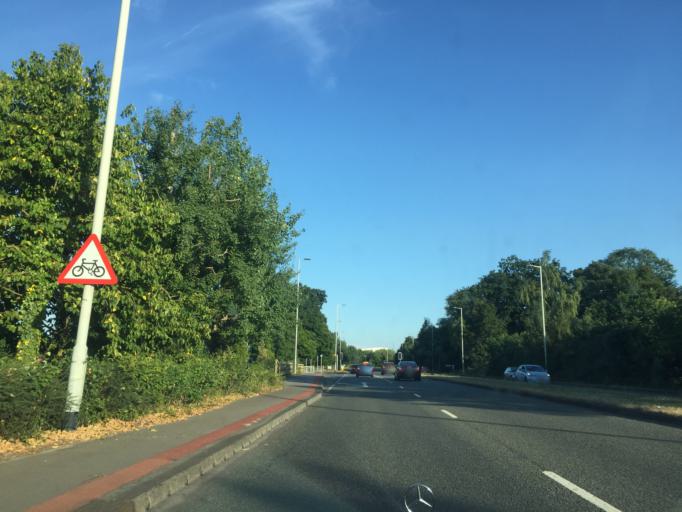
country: GB
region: England
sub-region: Bracknell Forest
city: Sandhurst
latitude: 51.3361
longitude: -0.7779
